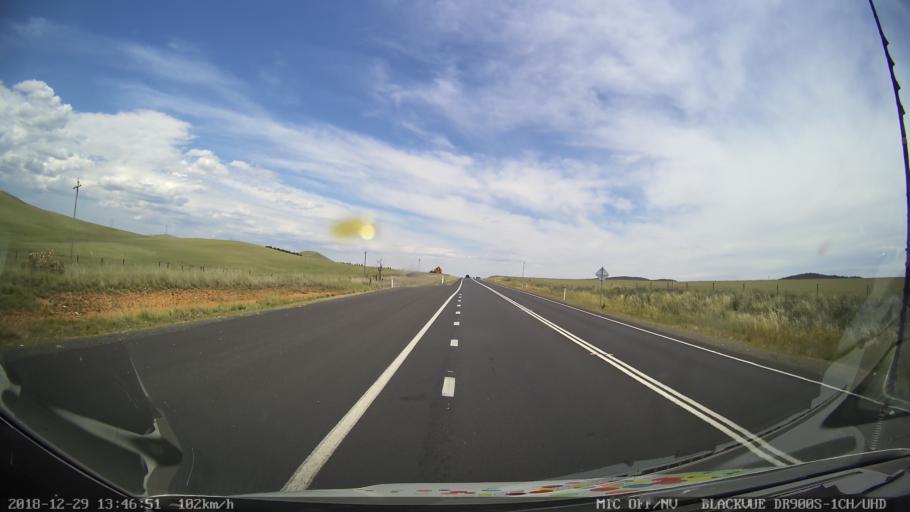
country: AU
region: New South Wales
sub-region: Cooma-Monaro
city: Cooma
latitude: -36.1177
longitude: 149.1418
